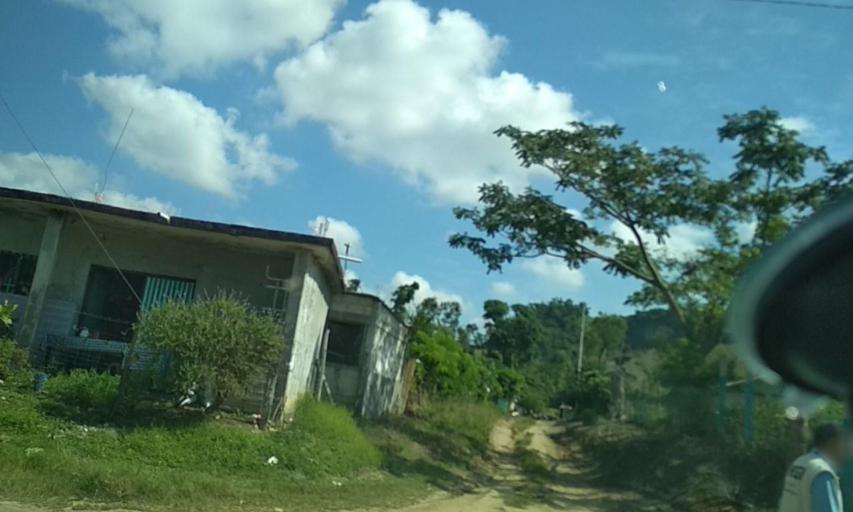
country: MX
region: Veracruz
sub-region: Cazones de Herrera
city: Rancho Nuevo
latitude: 20.6396
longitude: -97.2482
